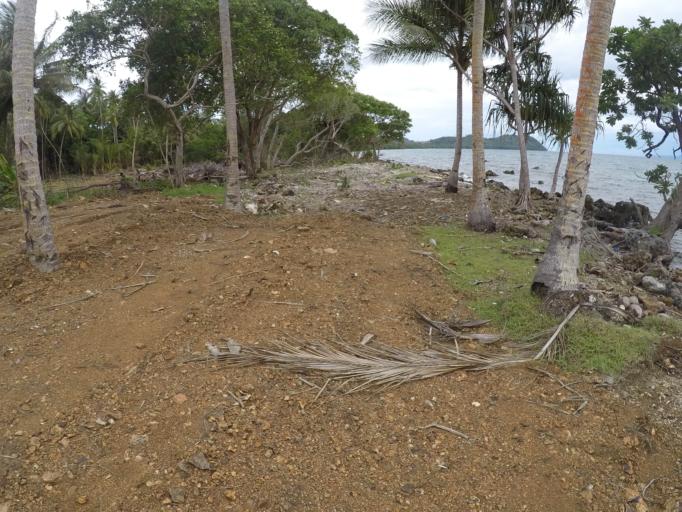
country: PG
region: Milne Bay
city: Alotau
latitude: -10.2630
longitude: 150.8112
